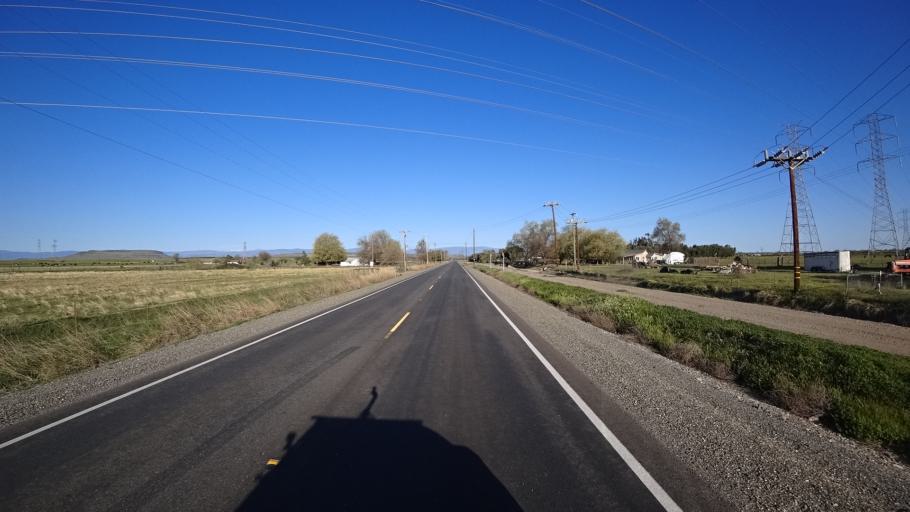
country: US
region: California
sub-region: Glenn County
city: Orland
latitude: 39.7725
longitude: -122.2649
